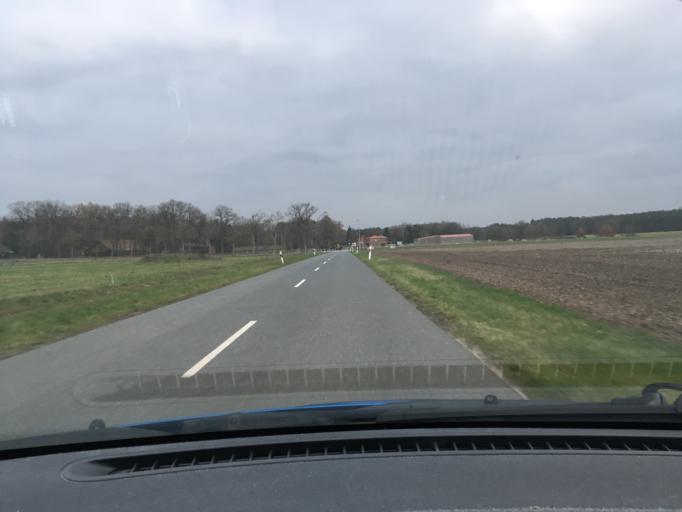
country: DE
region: Lower Saxony
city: Walsrode
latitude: 52.8307
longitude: 9.5728
